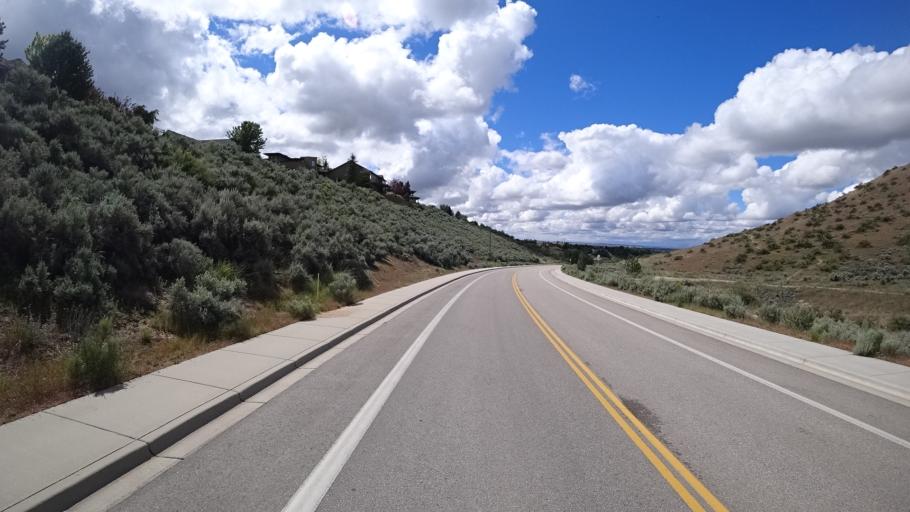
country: US
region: Idaho
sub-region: Ada County
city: Boise
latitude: 43.6575
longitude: -116.1895
